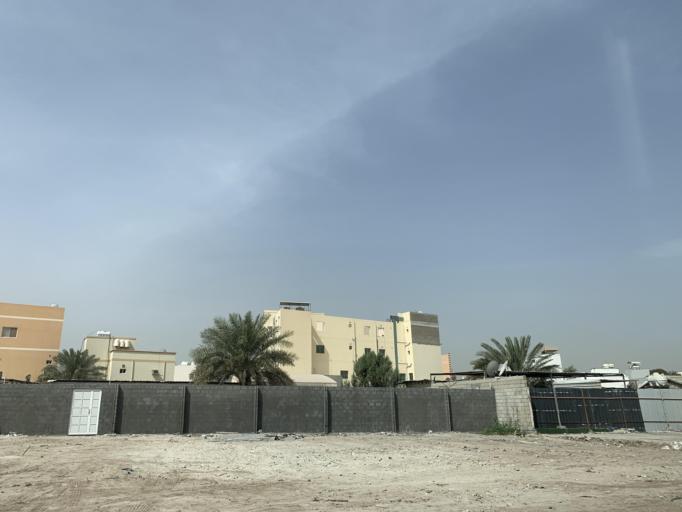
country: BH
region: Northern
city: Madinat `Isa
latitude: 26.1750
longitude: 50.5651
